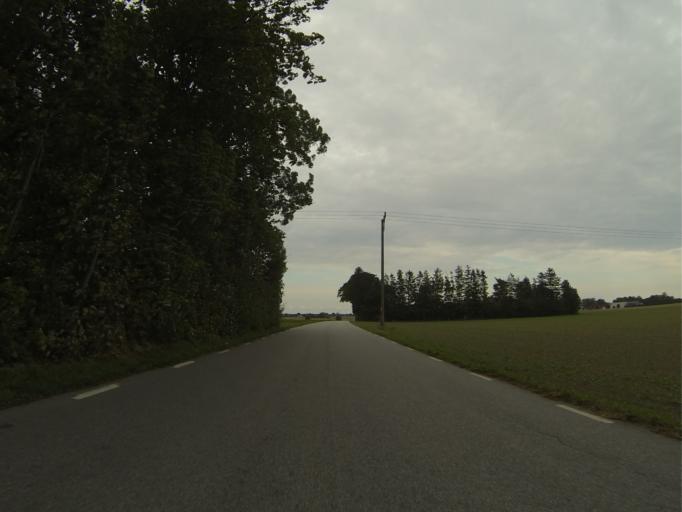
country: SE
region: Skane
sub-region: Staffanstorps Kommun
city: Hjaerup
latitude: 55.6519
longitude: 13.1569
